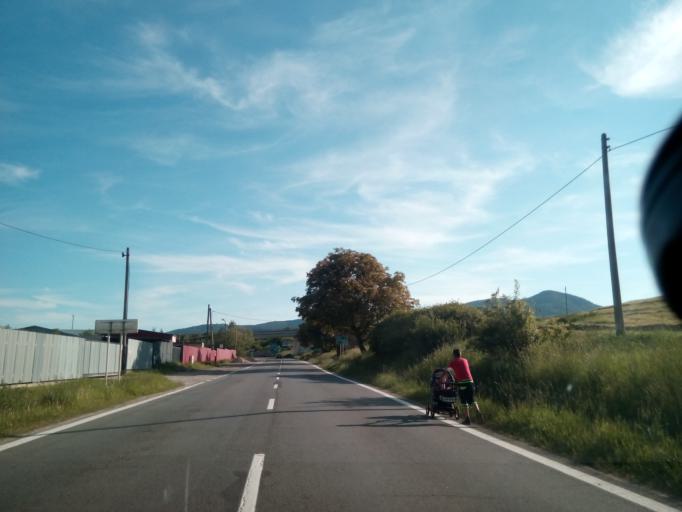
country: SK
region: Kosicky
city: Krompachy
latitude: 49.0114
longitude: 20.9441
